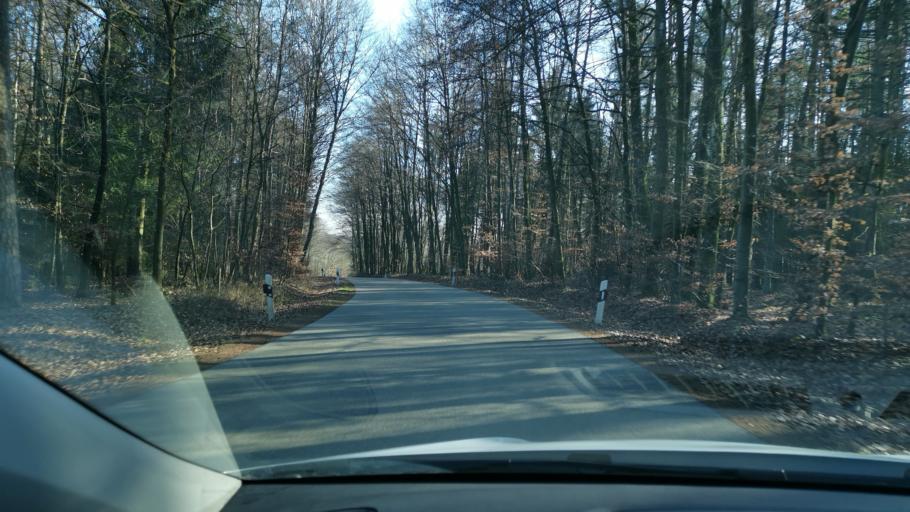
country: DE
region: Bavaria
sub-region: Swabia
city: Aindling
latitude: 48.5426
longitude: 10.9652
